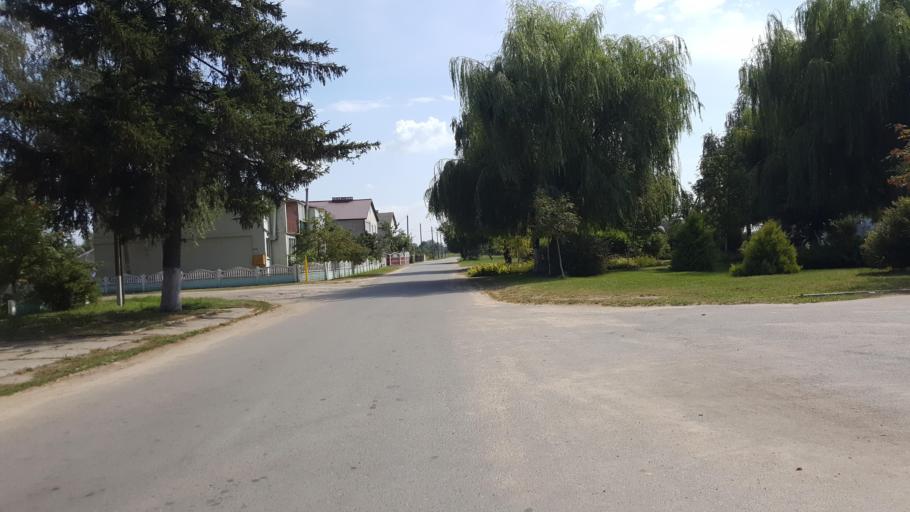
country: PL
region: Podlasie
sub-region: Powiat hajnowski
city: Czeremcha
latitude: 52.4977
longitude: 23.5695
